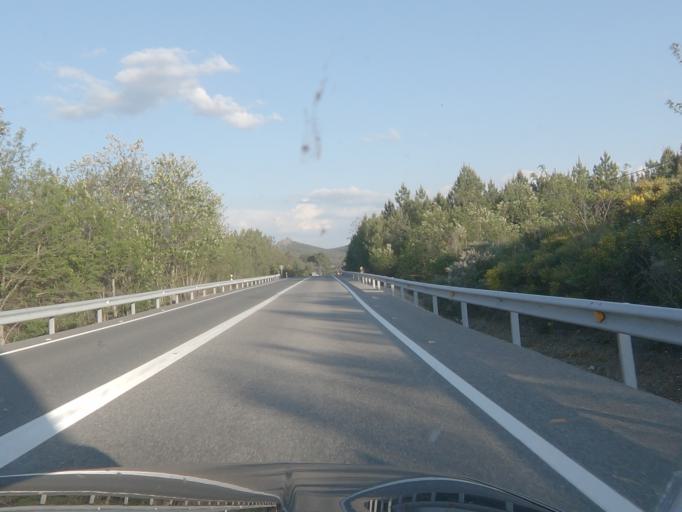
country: PT
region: Portalegre
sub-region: Portalegre
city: Sao Juliao
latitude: 39.3490
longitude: -7.3031
